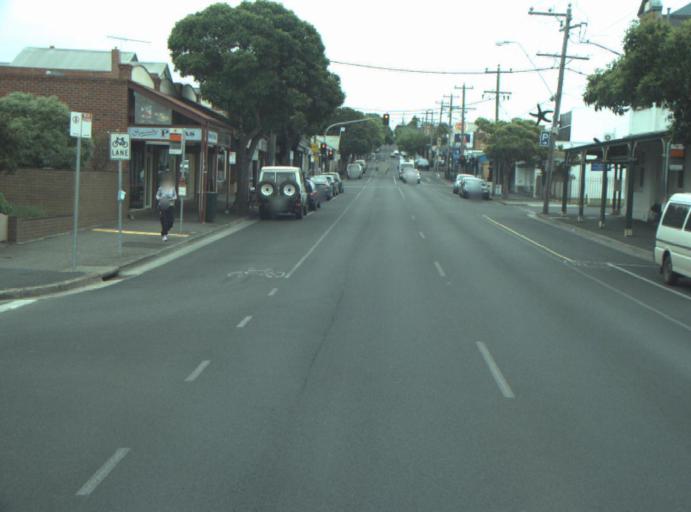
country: AU
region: Victoria
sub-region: Greater Geelong
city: Geelong
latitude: -38.1573
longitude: 144.3452
